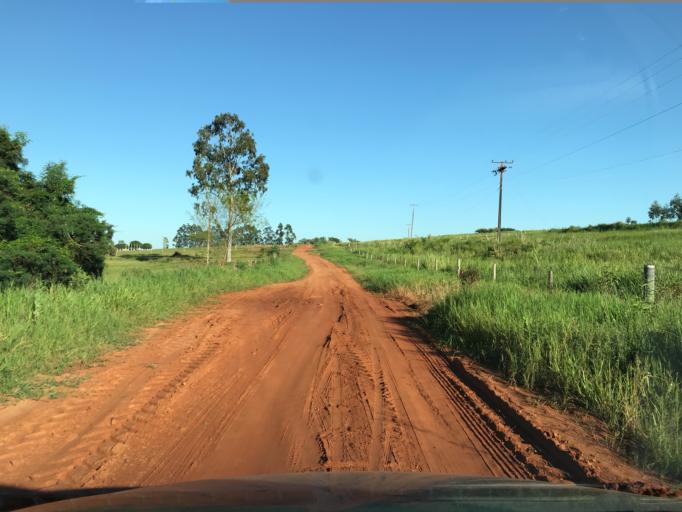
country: BR
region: Parana
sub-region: Ipora
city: Ipora
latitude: -23.9940
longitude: -53.7280
